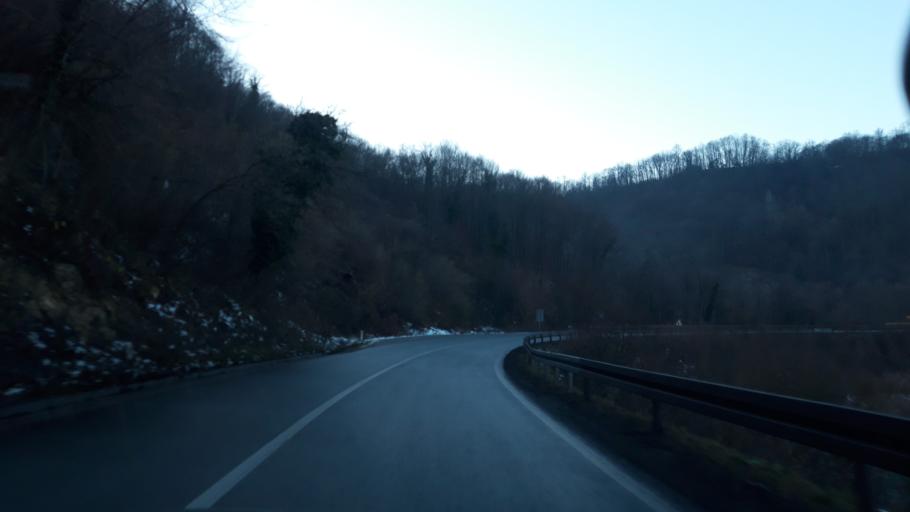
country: RS
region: Central Serbia
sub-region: Macvanski Okrug
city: Mali Zvornik
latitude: 44.3188
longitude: 19.1260
